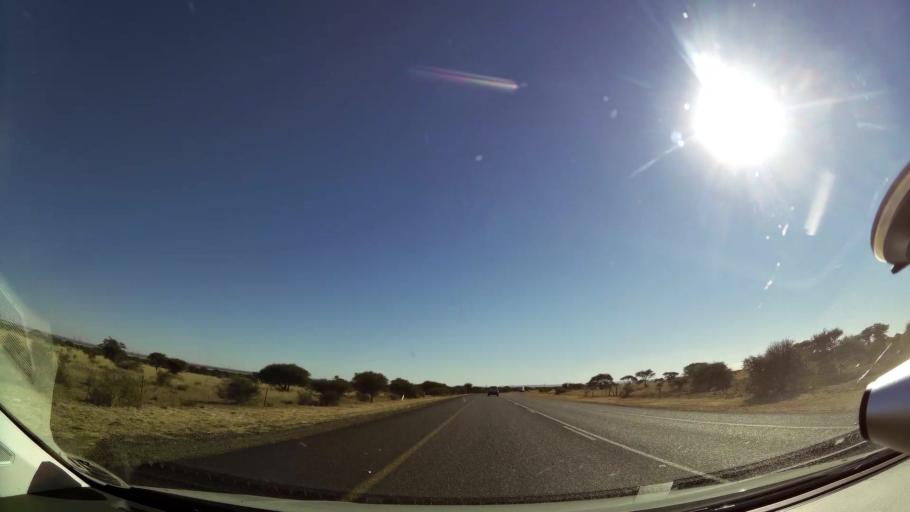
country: ZA
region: Northern Cape
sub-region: Frances Baard District Municipality
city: Kimberley
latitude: -28.5692
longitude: 24.7702
